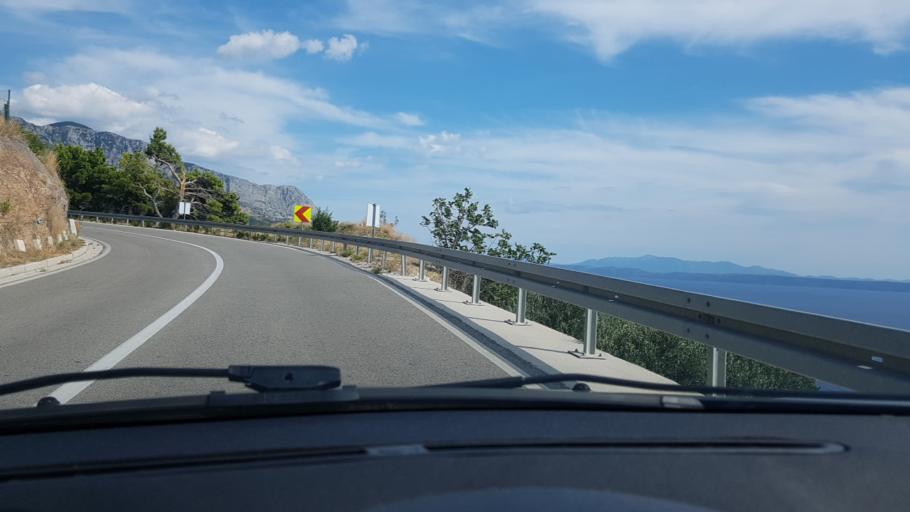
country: HR
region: Splitsko-Dalmatinska
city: Tucepi
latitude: 43.2785
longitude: 17.0470
